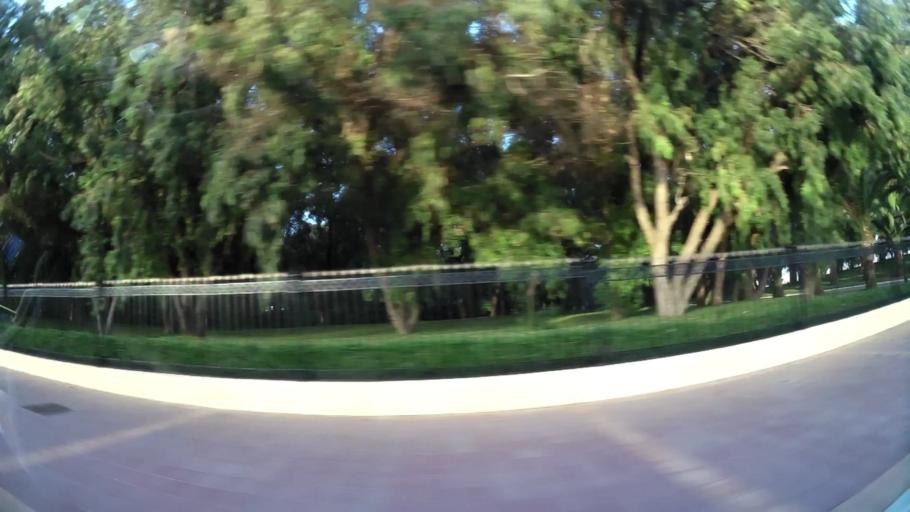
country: MA
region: Souss-Massa-Draa
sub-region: Agadir-Ida-ou-Tnan
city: Agadir
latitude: 30.4074
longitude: -9.5945
